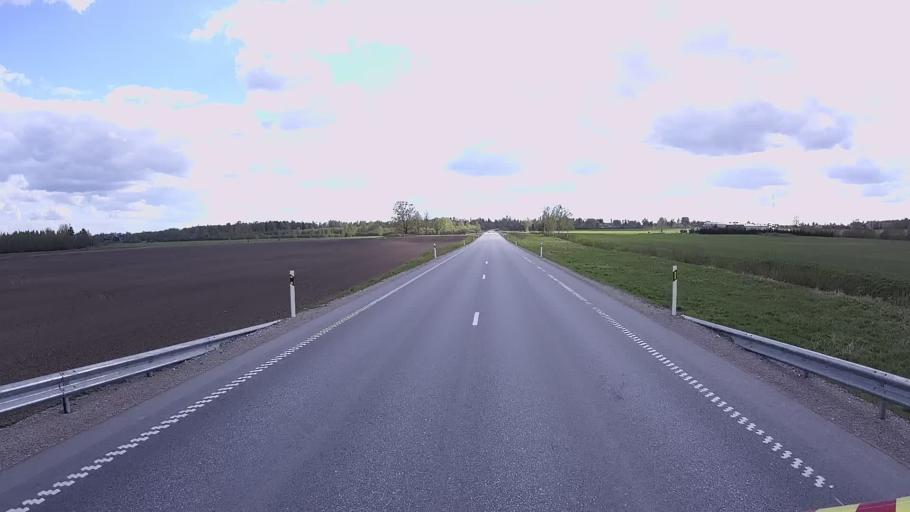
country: EE
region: Jogevamaa
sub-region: Mustvee linn
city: Mustvee
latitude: 58.8246
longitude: 26.7514
